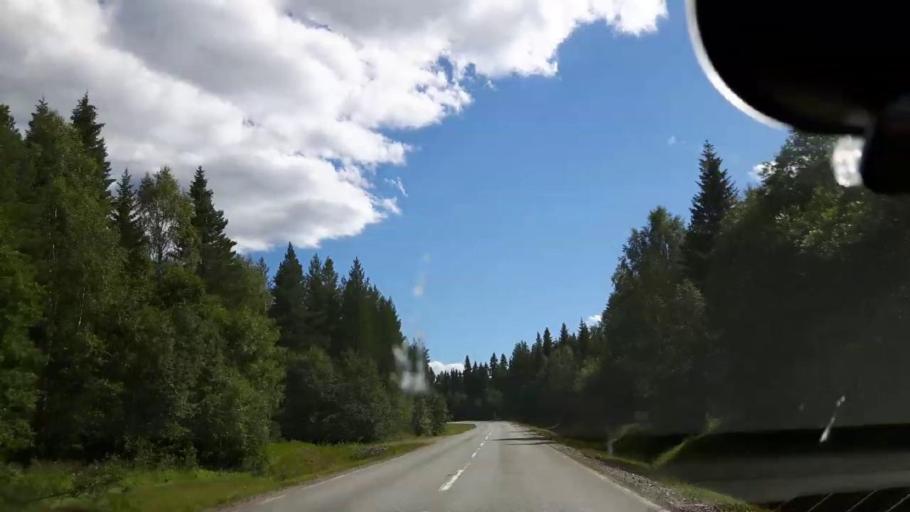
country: SE
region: Vaesternorrland
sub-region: Ange Kommun
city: Fransta
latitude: 62.8166
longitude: 16.2048
